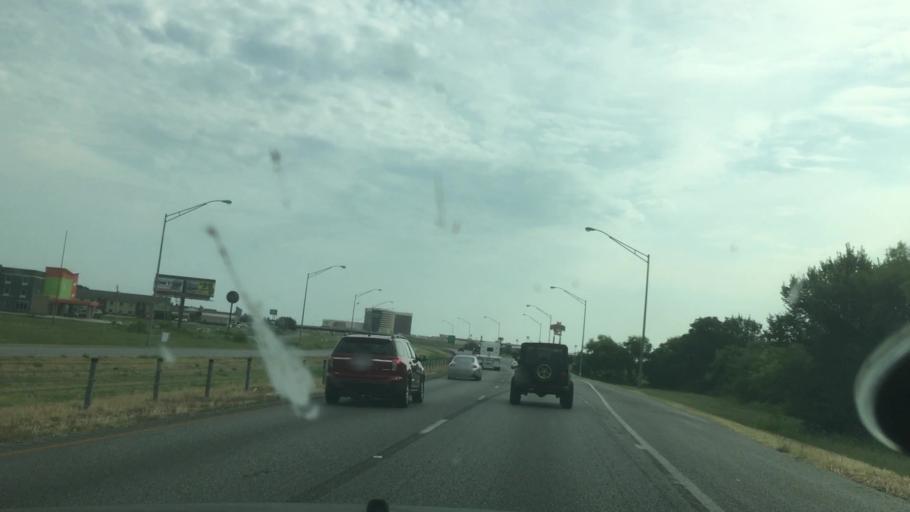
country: US
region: Oklahoma
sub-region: Bryan County
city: Calera
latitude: 33.9405
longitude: -96.4200
